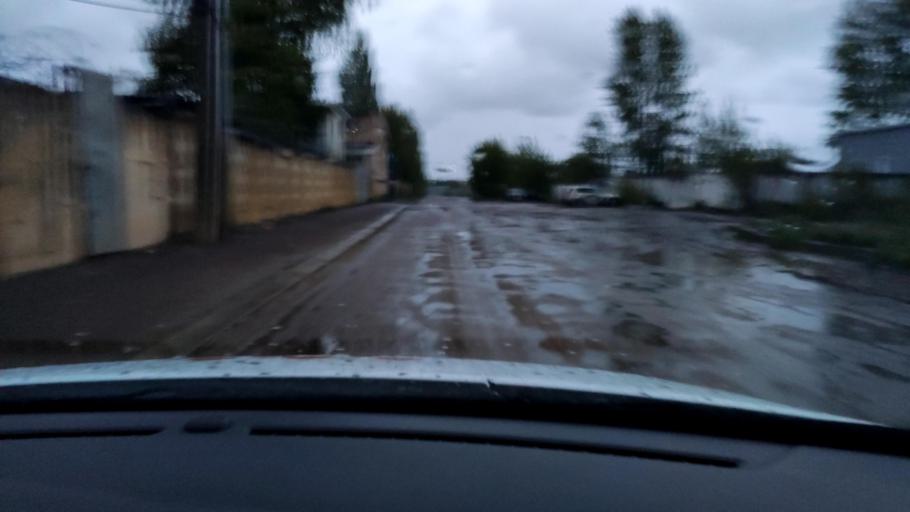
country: RU
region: Tatarstan
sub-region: Gorod Kazan'
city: Kazan
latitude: 55.7205
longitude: 49.1241
